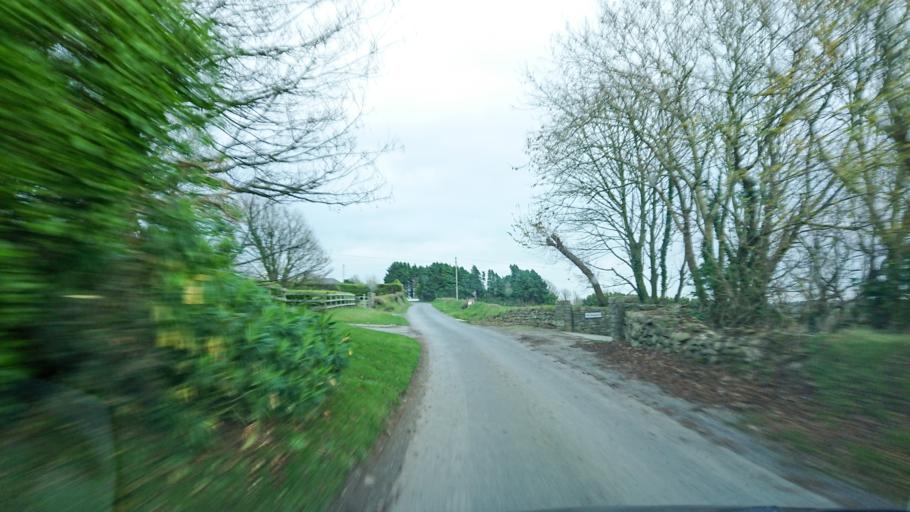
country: IE
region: Munster
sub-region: Waterford
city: Dunmore East
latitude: 52.2486
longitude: -7.0054
